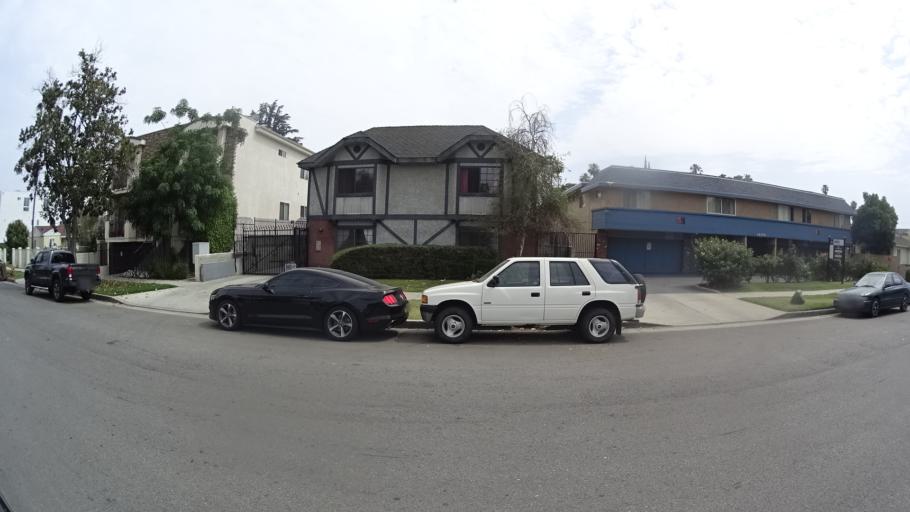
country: US
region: California
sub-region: Los Angeles County
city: Van Nuys
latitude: 34.1847
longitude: -118.4553
